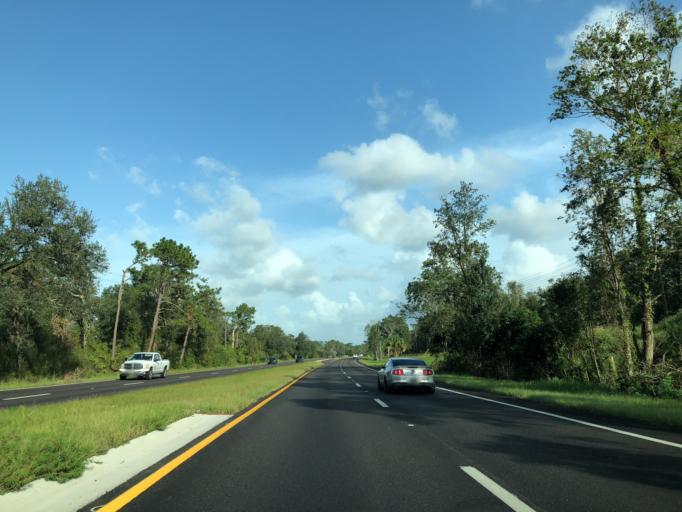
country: US
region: Florida
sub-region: Orange County
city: Bithlo
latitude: 28.5652
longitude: -81.1469
